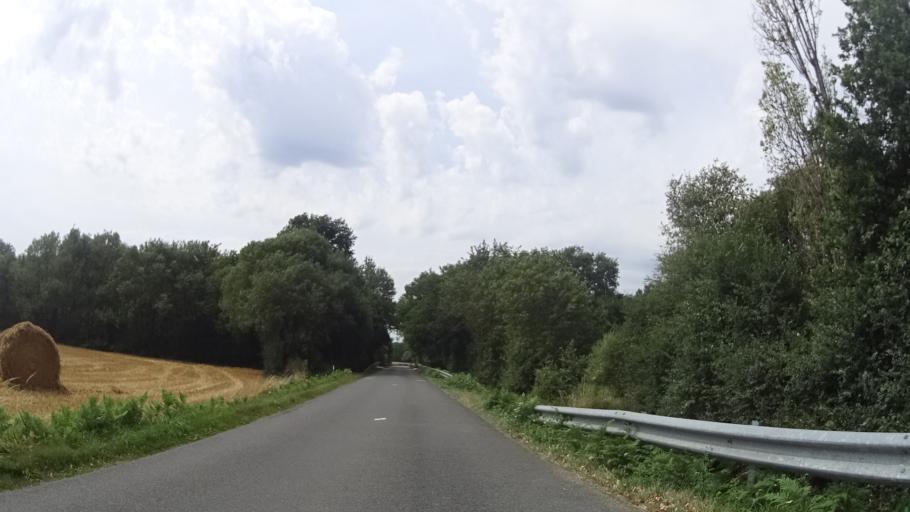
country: FR
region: Pays de la Loire
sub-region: Departement de la Loire-Atlantique
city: Heric
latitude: 47.4511
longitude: -1.7022
